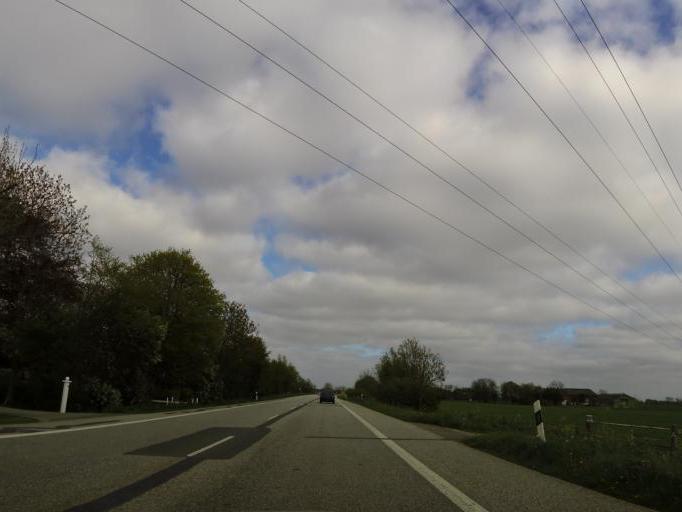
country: DE
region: Schleswig-Holstein
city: Stedesand
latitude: 54.7509
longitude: 8.9045
